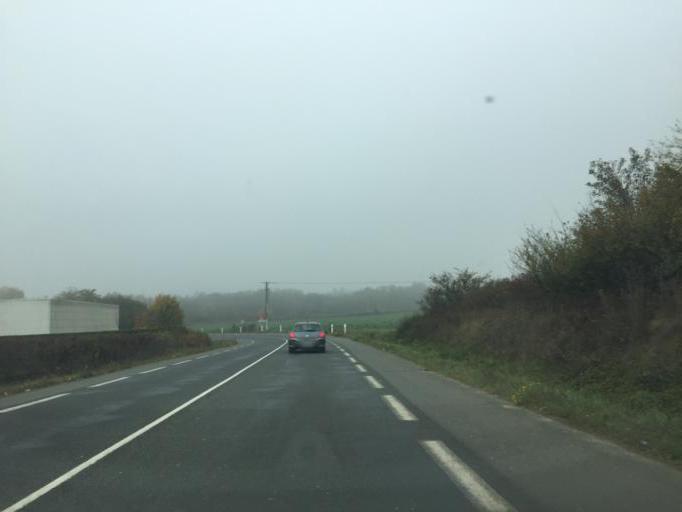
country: FR
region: Rhone-Alpes
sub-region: Departement du Rhone
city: Rillieux-la-Pape
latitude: 45.8243
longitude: 4.9220
